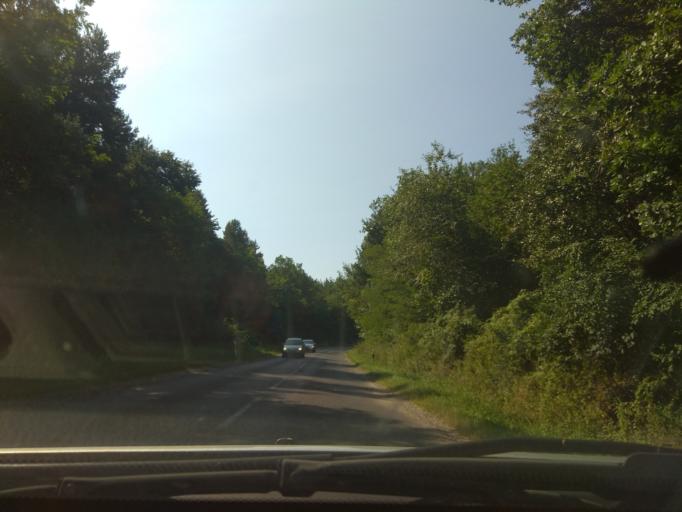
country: HU
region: Borsod-Abauj-Zemplen
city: Harsany
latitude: 47.9924
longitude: 20.7541
